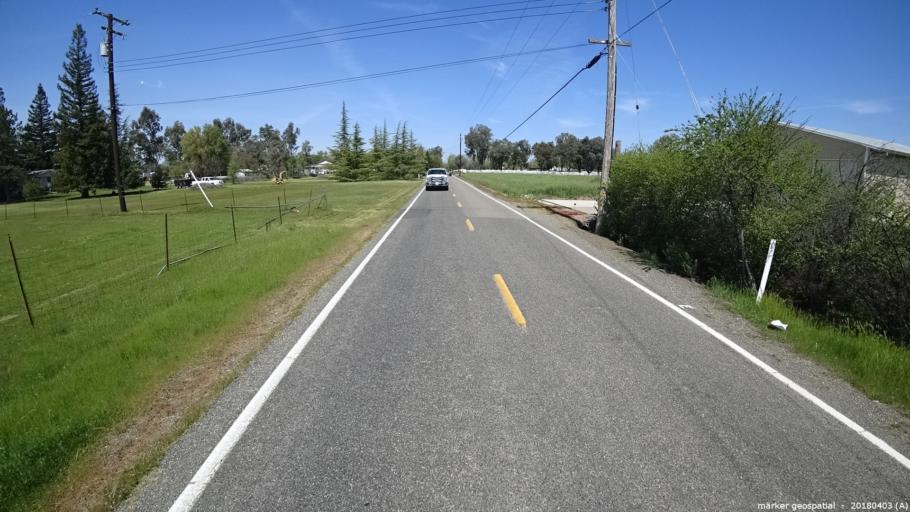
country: US
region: California
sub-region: Sacramento County
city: Wilton
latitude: 38.3805
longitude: -121.2608
